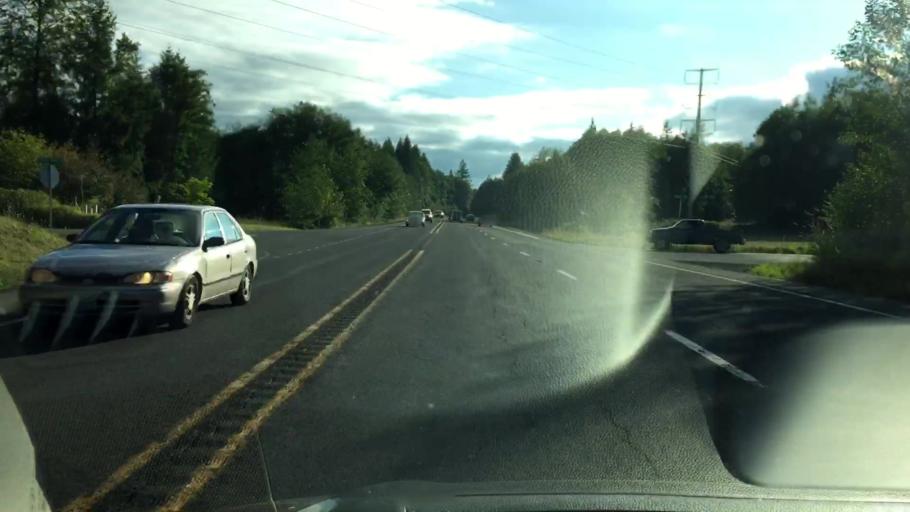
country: US
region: Washington
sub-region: Lewis County
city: Morton
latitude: 46.5446
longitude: -122.3492
